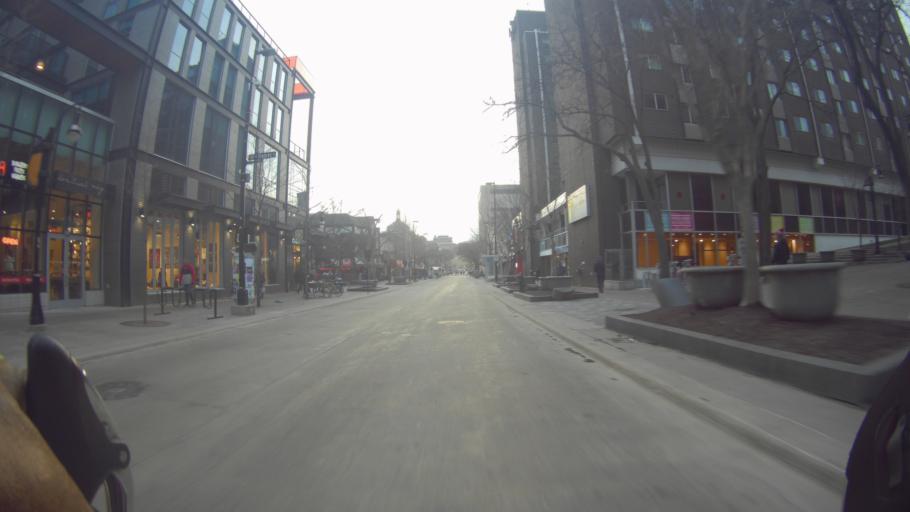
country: US
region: Wisconsin
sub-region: Dane County
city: Madison
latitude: 43.0749
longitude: -89.3953
